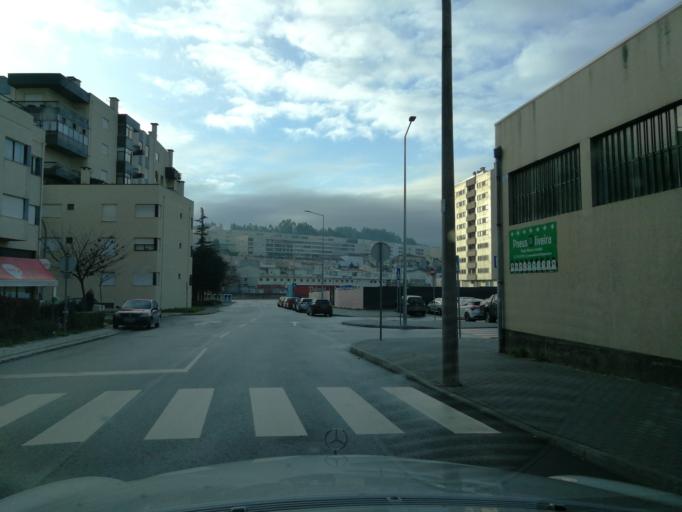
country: PT
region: Braga
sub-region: Braga
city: Braga
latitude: 41.5424
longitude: -8.4297
